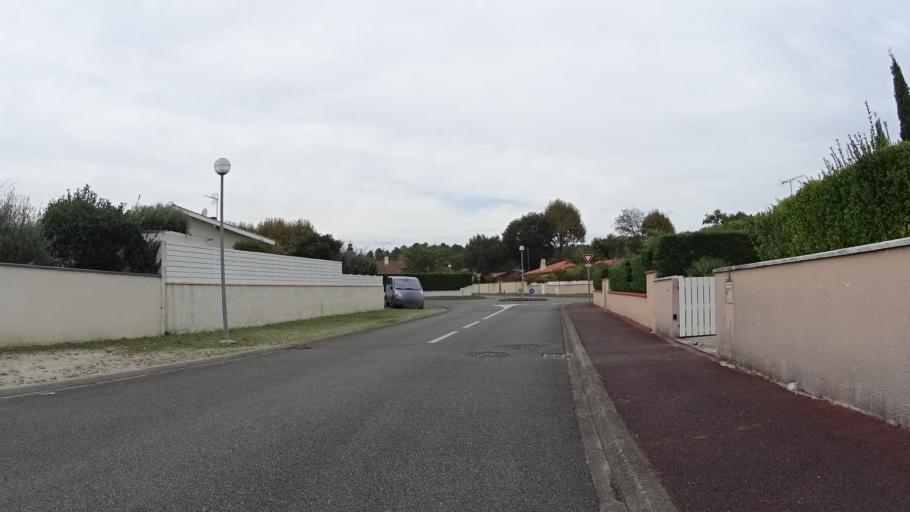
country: FR
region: Aquitaine
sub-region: Departement des Landes
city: Saint-Paul-les-Dax
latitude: 43.7298
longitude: -1.0857
